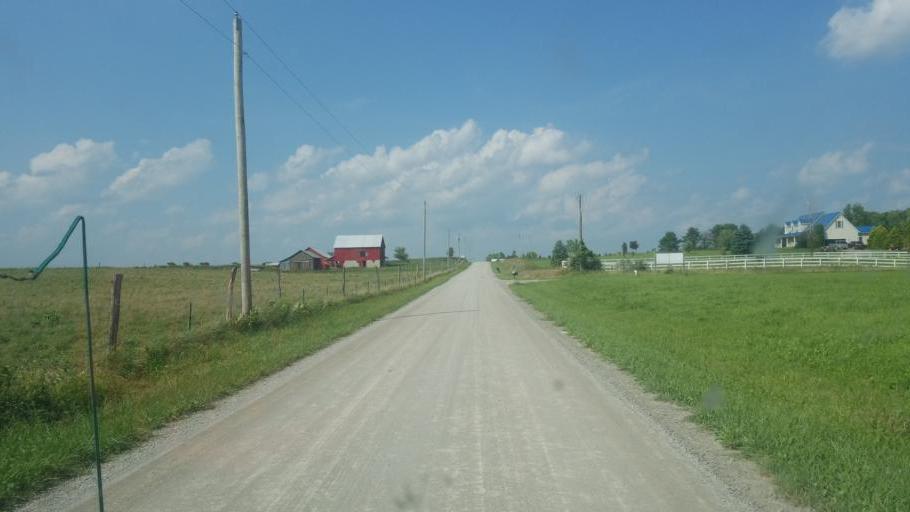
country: US
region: Ohio
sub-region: Wayne County
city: West Salem
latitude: 41.0479
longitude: -82.1448
